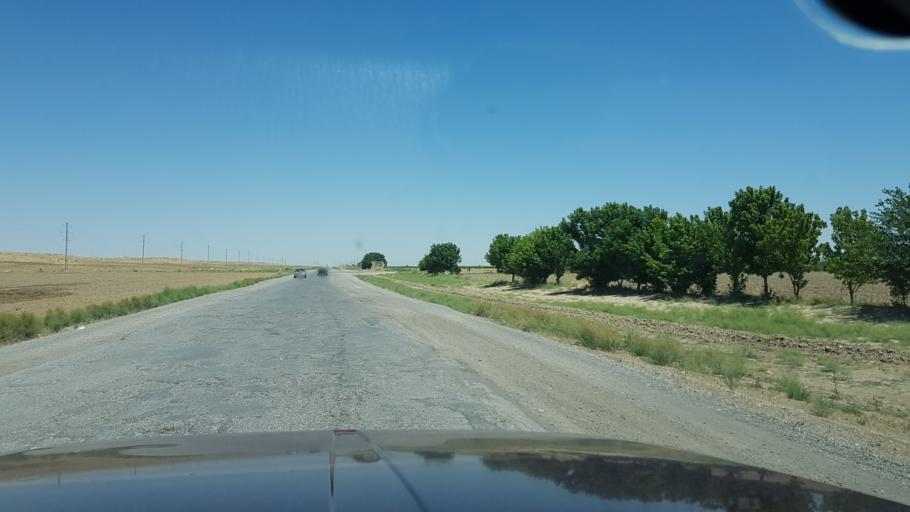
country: TM
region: Ahal
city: Annau
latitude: 37.8596
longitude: 58.7086
